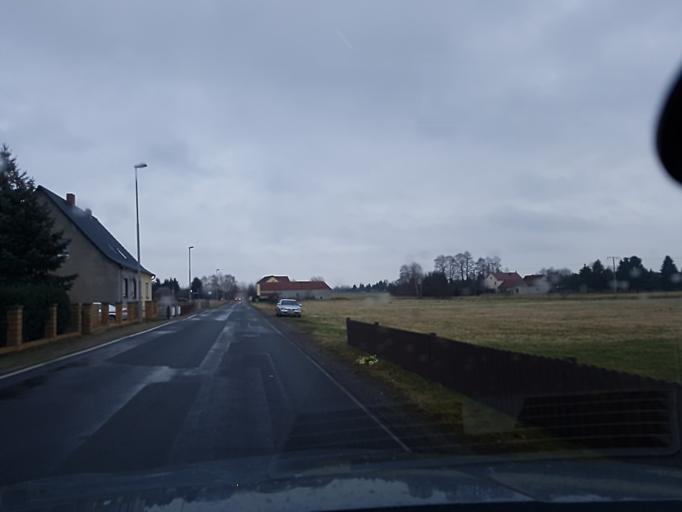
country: DE
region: Brandenburg
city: Schilda
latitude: 51.6097
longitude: 13.3852
